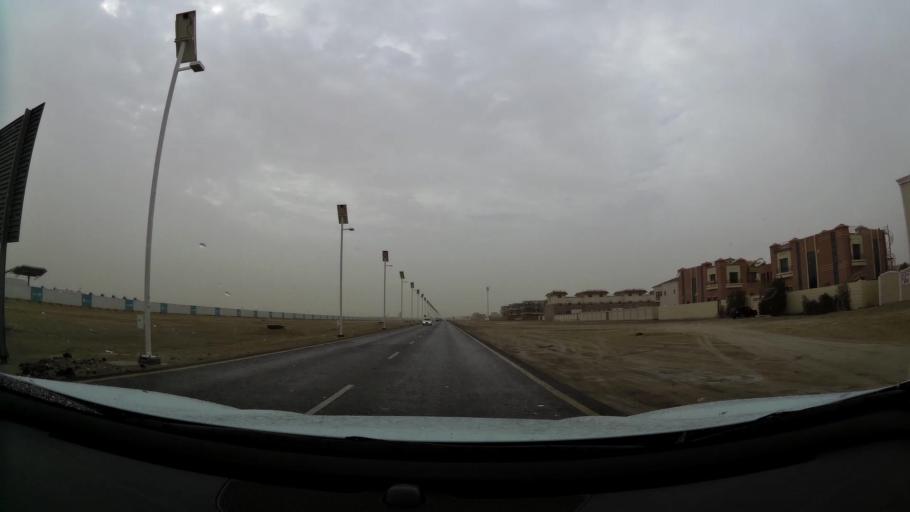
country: AE
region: Abu Dhabi
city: Abu Dhabi
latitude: 24.4304
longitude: 54.6048
